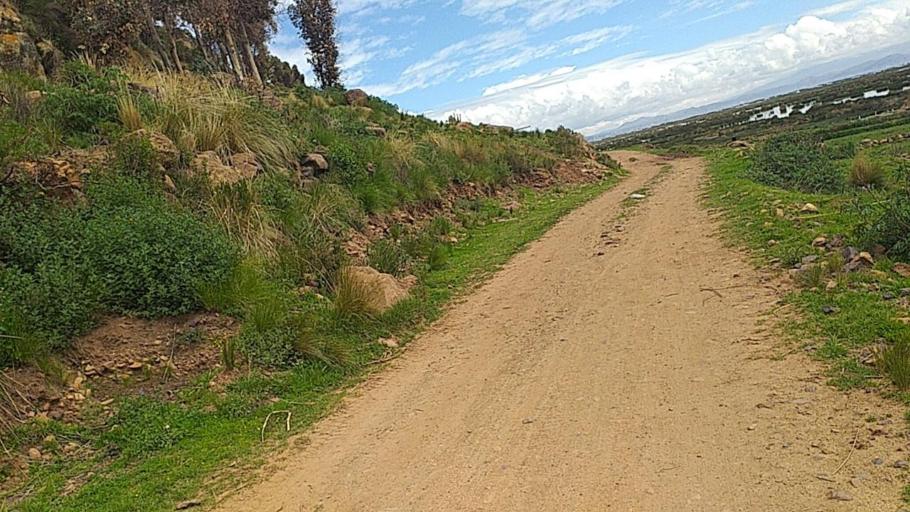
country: BO
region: La Paz
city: Batallas
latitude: -16.3343
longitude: -68.6379
